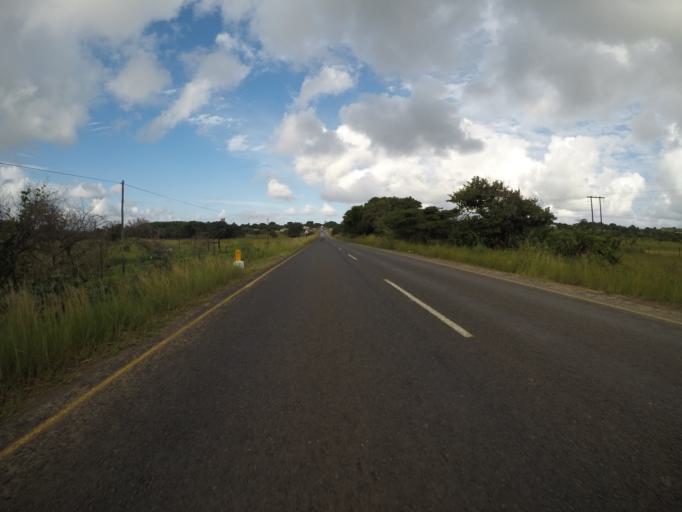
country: ZA
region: KwaZulu-Natal
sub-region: uMkhanyakude District Municipality
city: Mtubatuba
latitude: -28.3861
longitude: 32.3462
